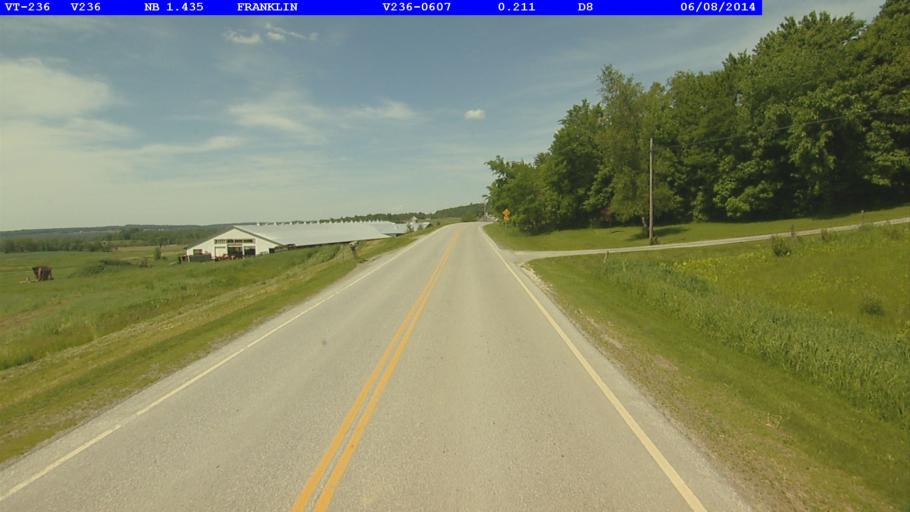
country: US
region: Vermont
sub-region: Franklin County
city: Enosburg Falls
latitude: 44.9315
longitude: -72.8657
